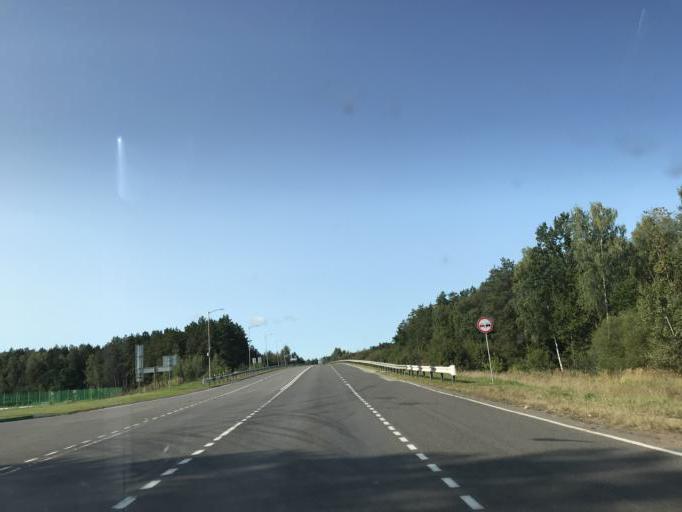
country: BY
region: Mogilev
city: Myazhysyatki
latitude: 53.8098
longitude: 30.2211
